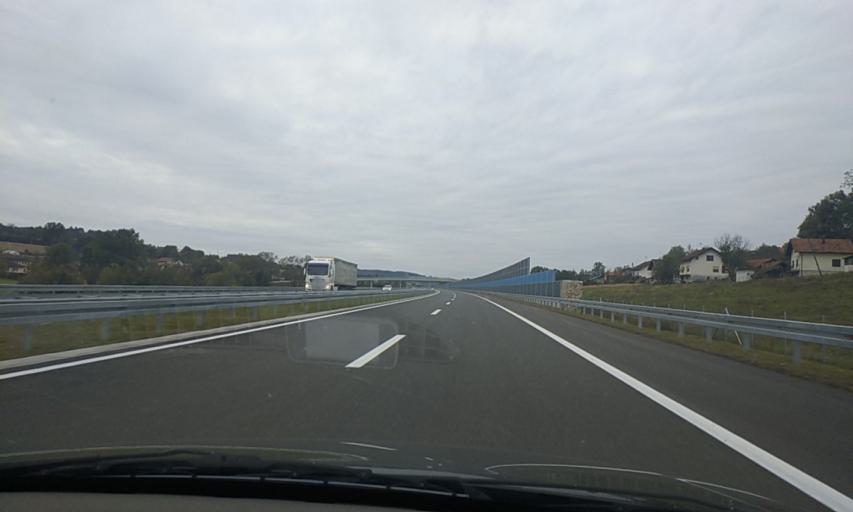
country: BA
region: Republika Srpska
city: Prnjavor
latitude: 44.8886
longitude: 17.5606
